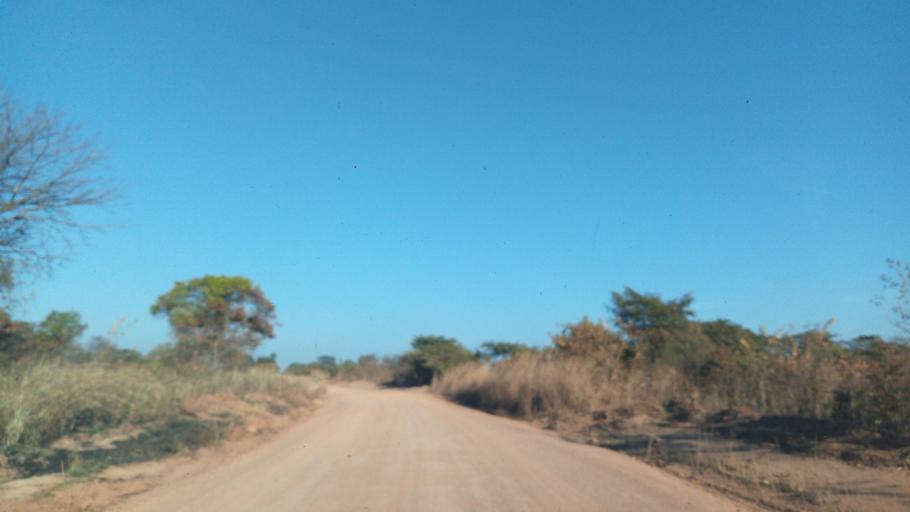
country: ZM
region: Luapula
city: Mwense
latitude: -10.4453
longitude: 28.5703
